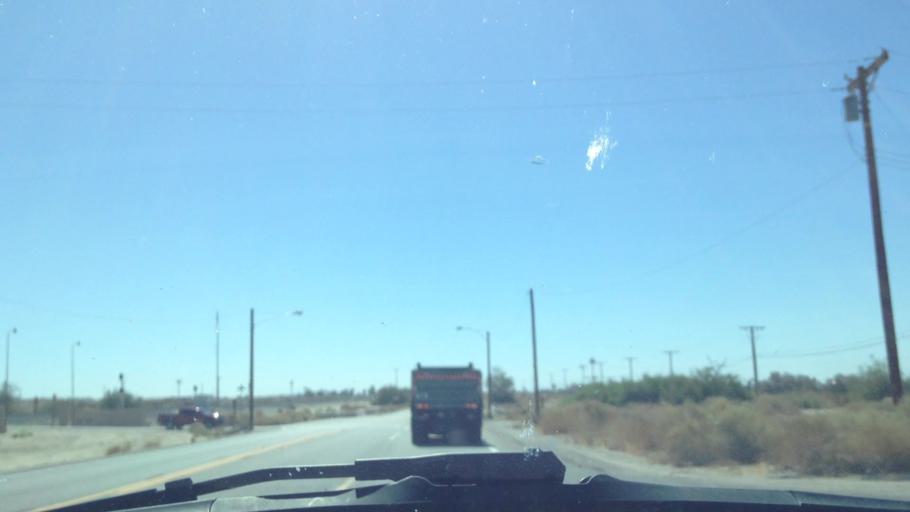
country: US
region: California
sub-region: Riverside County
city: Mecca
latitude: 33.5278
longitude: -115.9421
